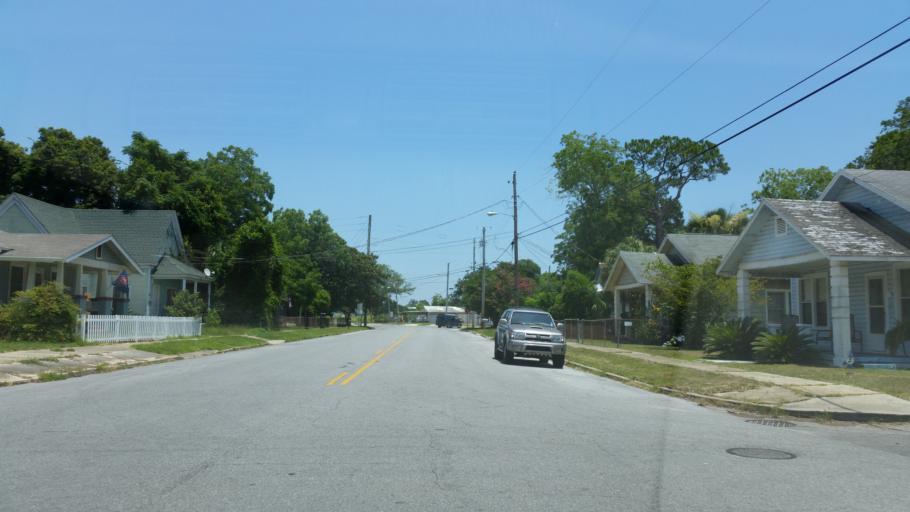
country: US
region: Florida
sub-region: Escambia County
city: Pensacola
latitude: 30.4072
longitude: -87.2276
